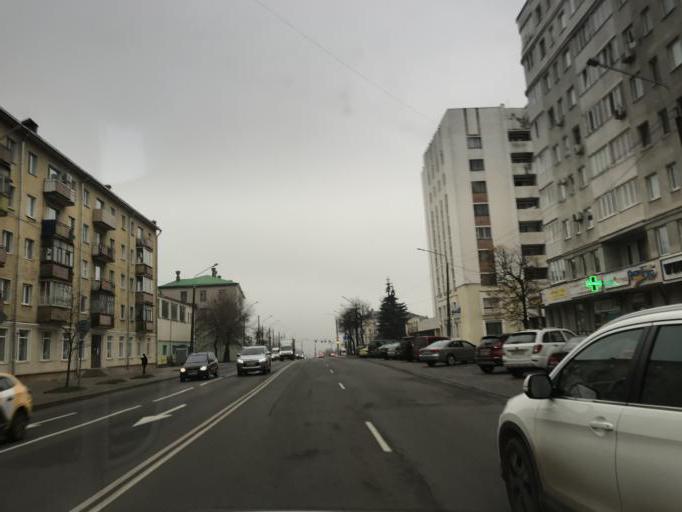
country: BY
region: Mogilev
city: Mahilyow
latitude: 53.8975
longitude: 30.3386
